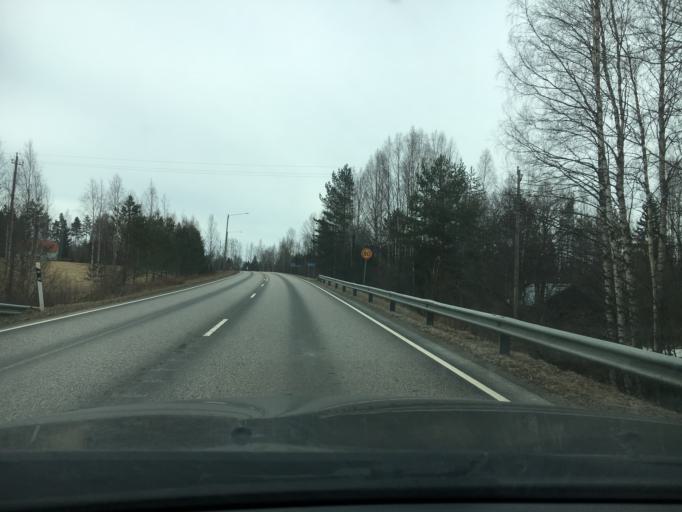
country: FI
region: Central Finland
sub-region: AEaenekoski
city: Konnevesi
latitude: 62.5860
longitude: 26.1830
